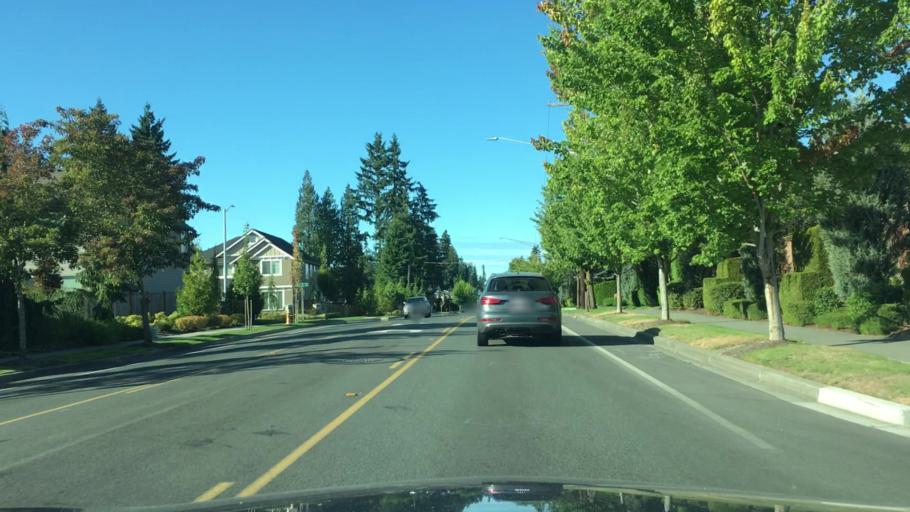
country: US
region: Washington
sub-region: Snohomish County
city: North Creek
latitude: 47.7962
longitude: -122.1811
